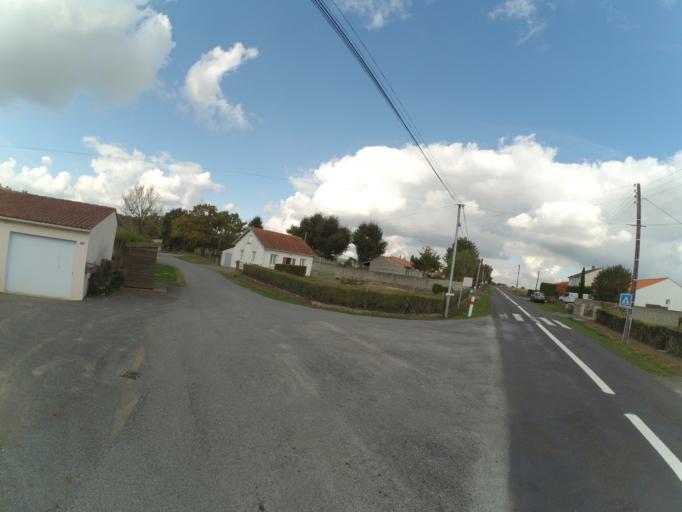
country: FR
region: Pays de la Loire
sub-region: Departement de la Loire-Atlantique
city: Remouille
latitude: 47.0629
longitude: -1.3575
